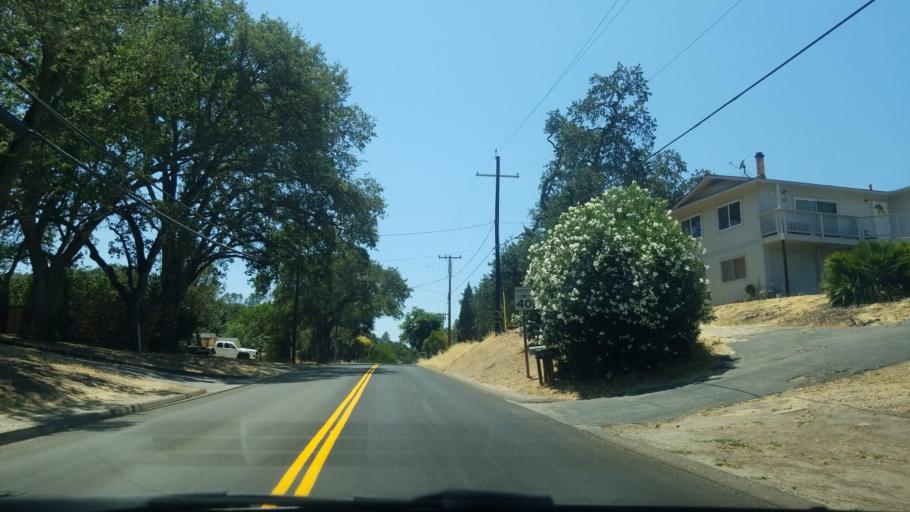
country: US
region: California
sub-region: San Luis Obispo County
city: Atascadero
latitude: 35.4856
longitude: -120.6493
